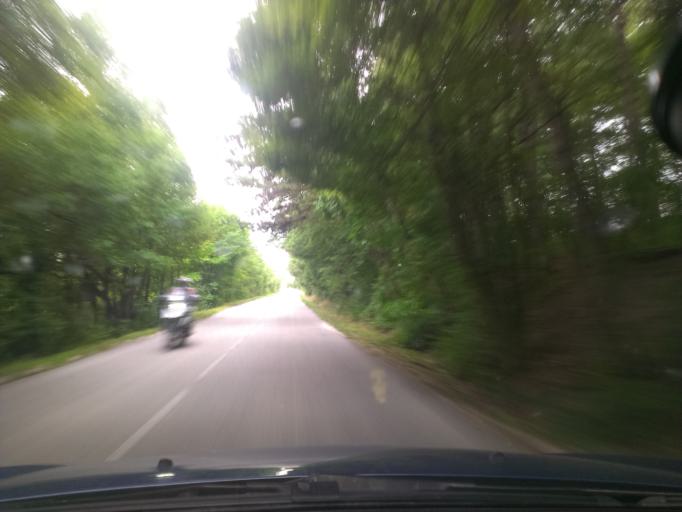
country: SK
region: Trnavsky
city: Vrbove
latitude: 48.6858
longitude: 17.6793
